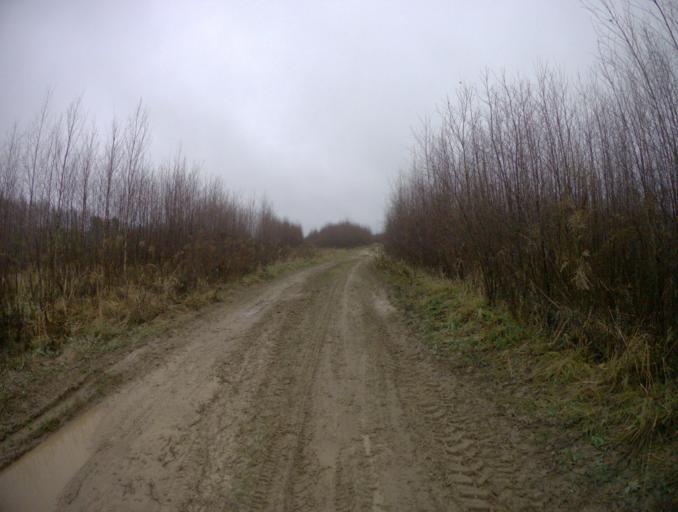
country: RU
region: Vladimir
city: Golovino
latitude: 55.9883
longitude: 40.4464
